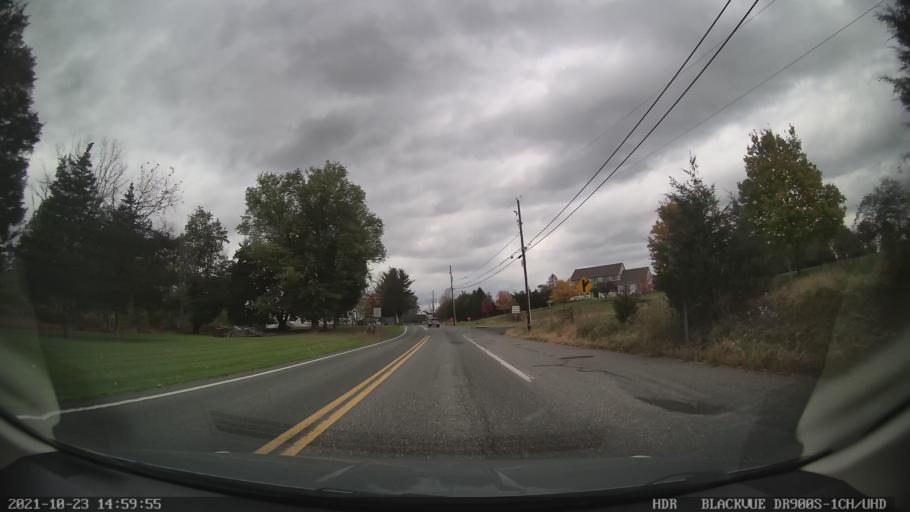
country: US
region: Pennsylvania
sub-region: Montgomery County
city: East Greenville
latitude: 40.3932
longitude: -75.5339
